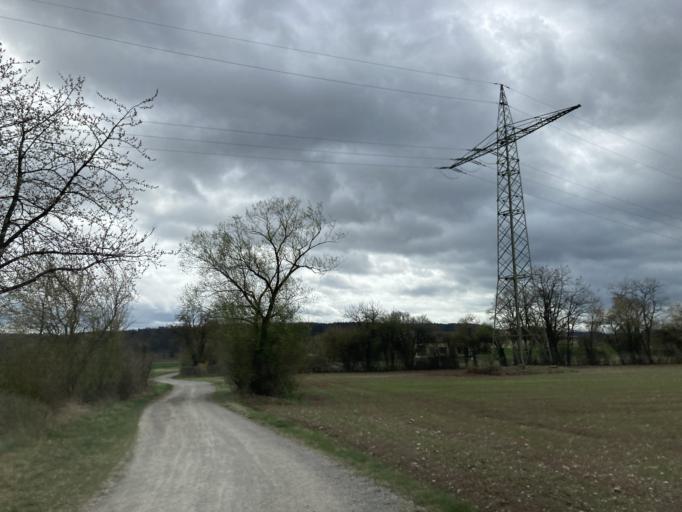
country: DE
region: Baden-Wuerttemberg
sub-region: Tuebingen Region
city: Tuebingen
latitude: 48.4978
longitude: 9.0151
